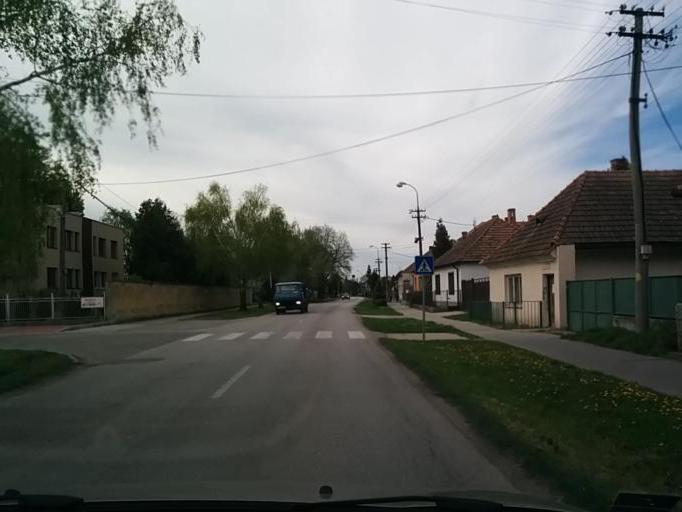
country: SK
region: Trnavsky
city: Sladkovicovo
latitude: 48.2330
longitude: 17.5678
